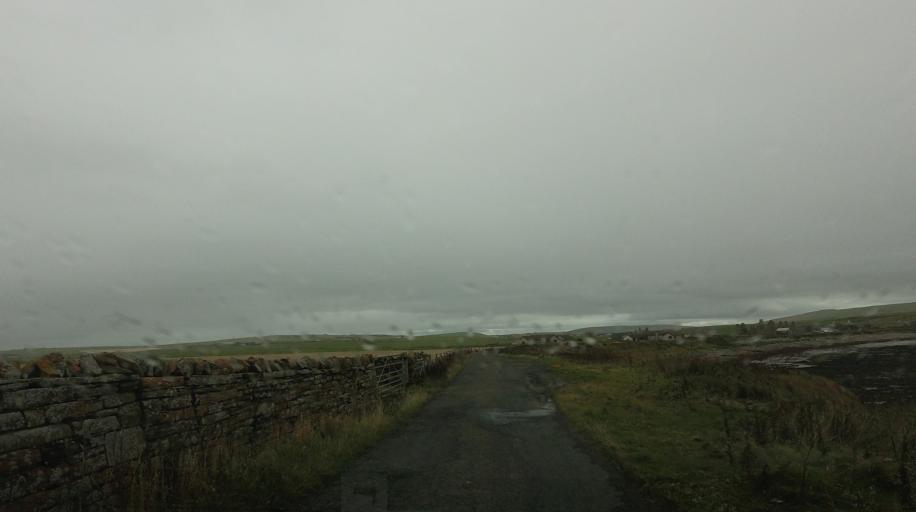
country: GB
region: Scotland
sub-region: Orkney Islands
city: Stromness
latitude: 59.1335
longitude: -3.3199
